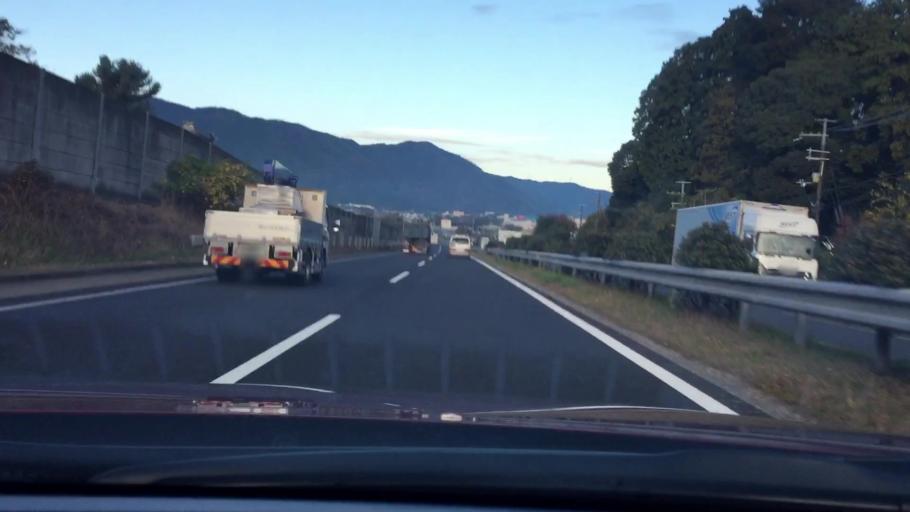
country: JP
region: Hyogo
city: Yamazakicho-nakabirose
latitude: 34.9965
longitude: 134.5607
